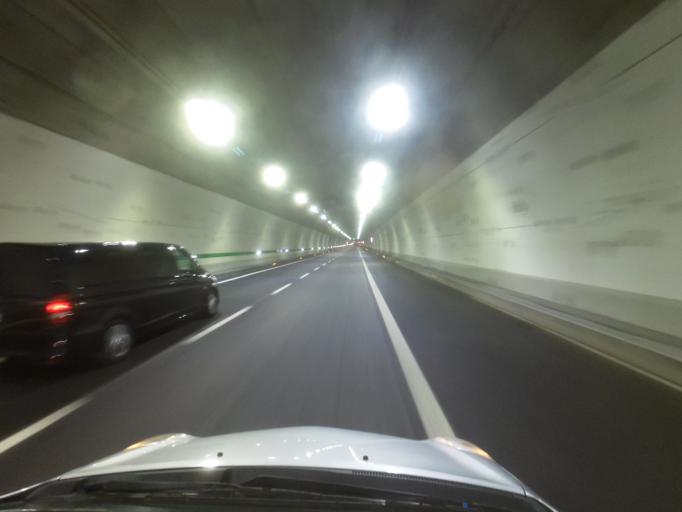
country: IT
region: Emilia-Romagna
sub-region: Provincia di Bologna
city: San Benedetto Val di Sambro
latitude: 44.1876
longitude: 11.1988
